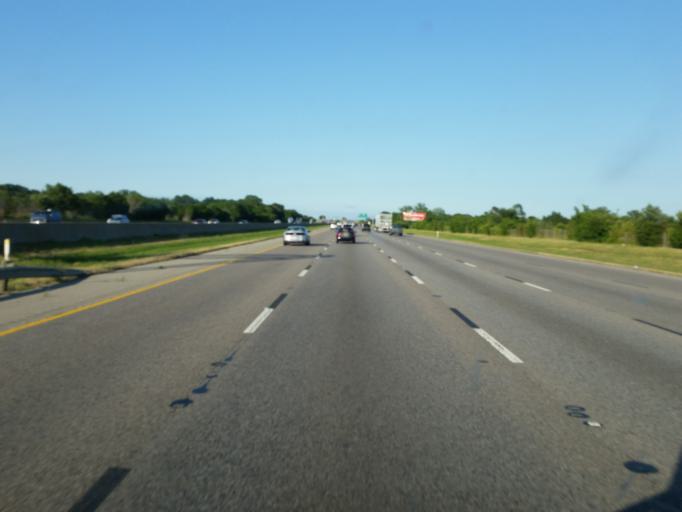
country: US
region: Texas
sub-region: Dallas County
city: Balch Springs
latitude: 32.6835
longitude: -96.6539
